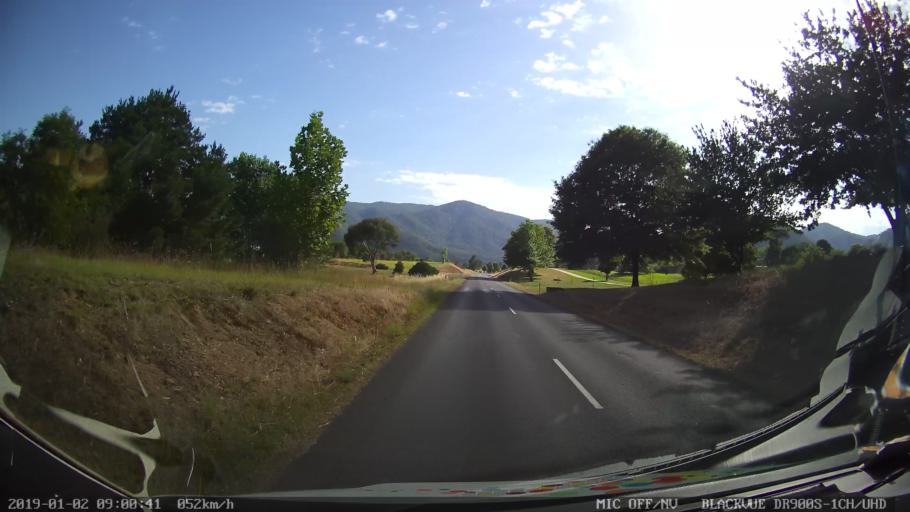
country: AU
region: New South Wales
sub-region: Tumut Shire
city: Tumut
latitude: -35.5797
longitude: 148.2990
